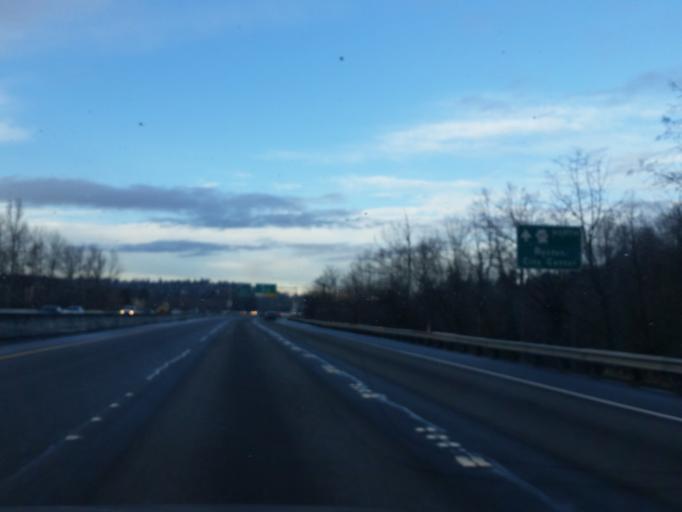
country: US
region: Washington
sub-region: King County
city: Renton
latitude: 47.4601
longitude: -122.2173
